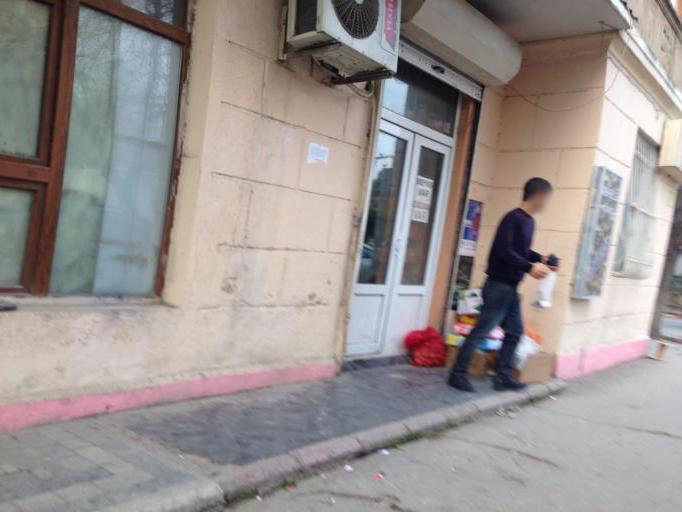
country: AZ
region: Baki
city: Baku
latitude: 40.4005
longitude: 49.8720
